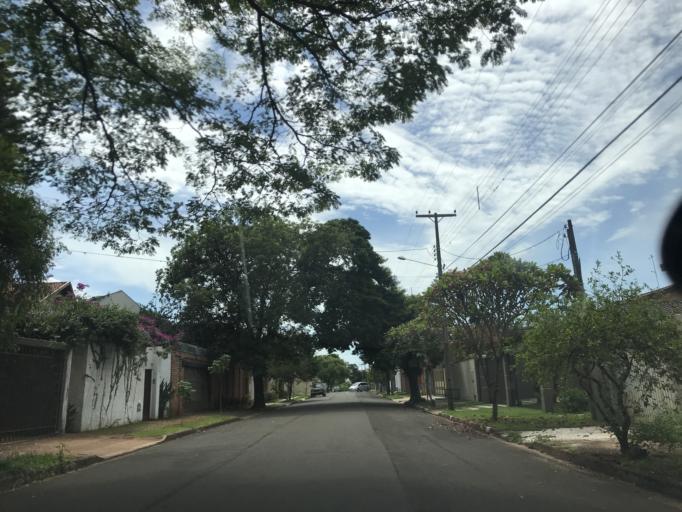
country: BR
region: Parana
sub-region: Londrina
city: Londrina
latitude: -23.3444
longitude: -51.1550
